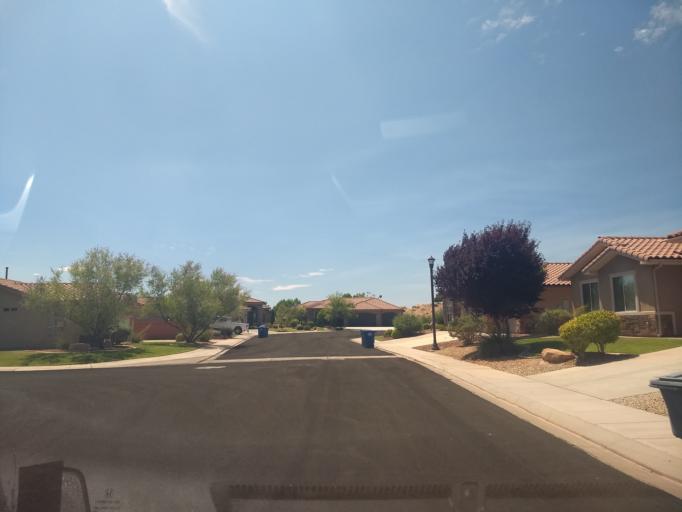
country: US
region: Utah
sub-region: Washington County
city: Washington
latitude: 37.1438
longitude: -113.4826
